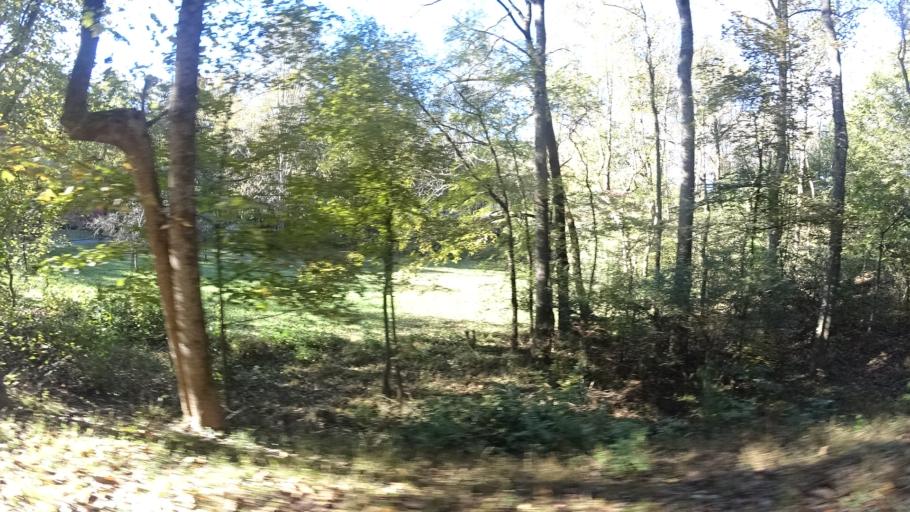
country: US
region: Tennessee
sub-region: Knox County
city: Knoxville
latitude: 35.9083
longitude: -83.9902
